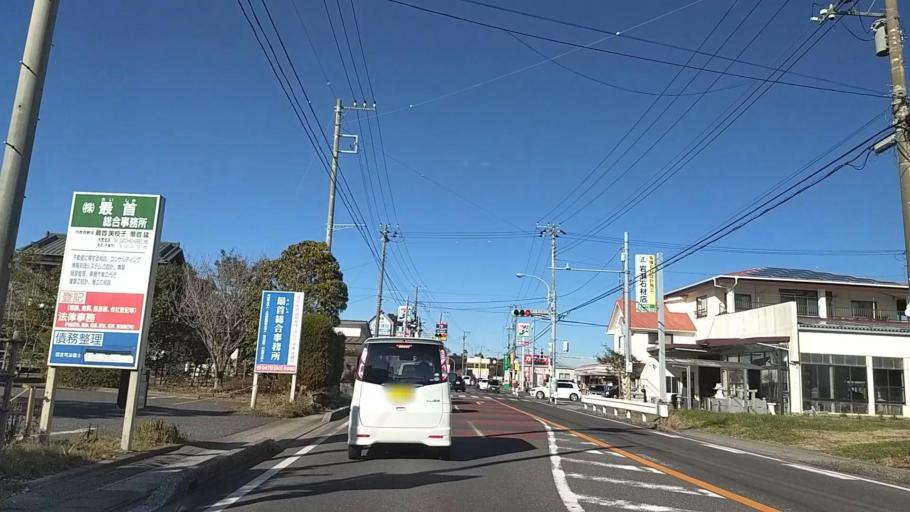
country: JP
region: Chiba
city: Ohara
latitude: 35.2578
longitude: 140.3937
